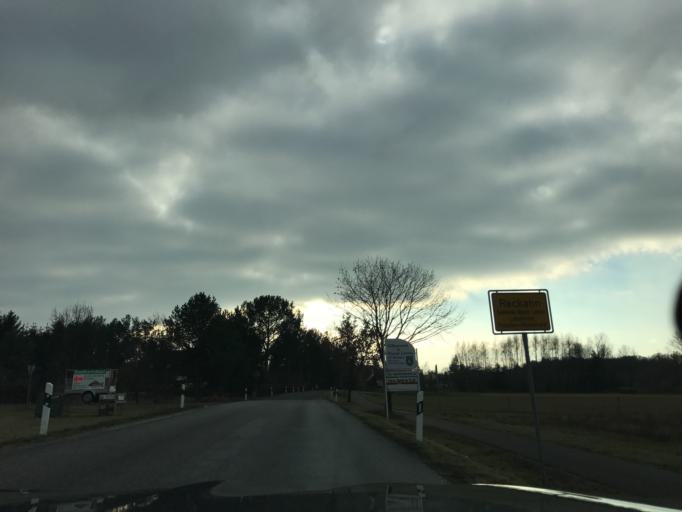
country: DE
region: Brandenburg
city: Brandenburg an der Havel
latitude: 52.3408
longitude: 12.5479
